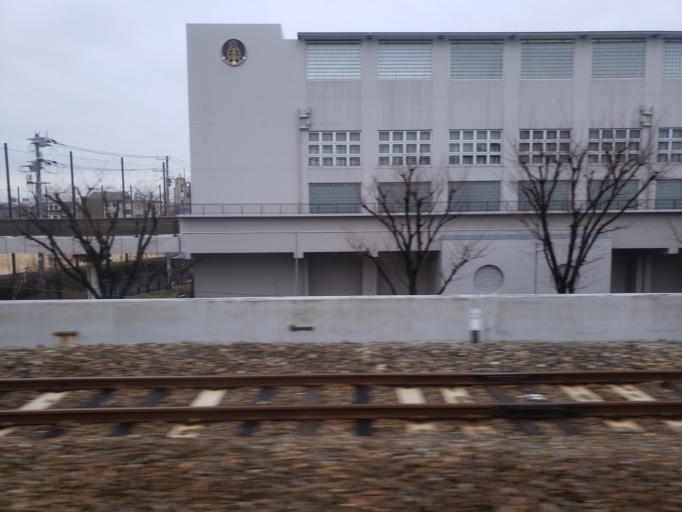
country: JP
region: Hyogo
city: Kobe
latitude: 34.6618
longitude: 135.1531
